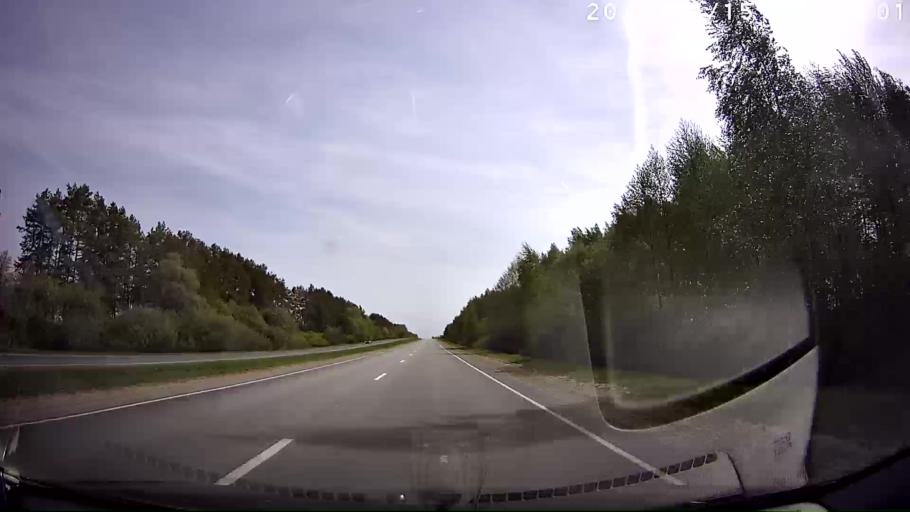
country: RU
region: Mariy-El
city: Sovetskiy
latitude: 56.7400
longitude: 48.1809
